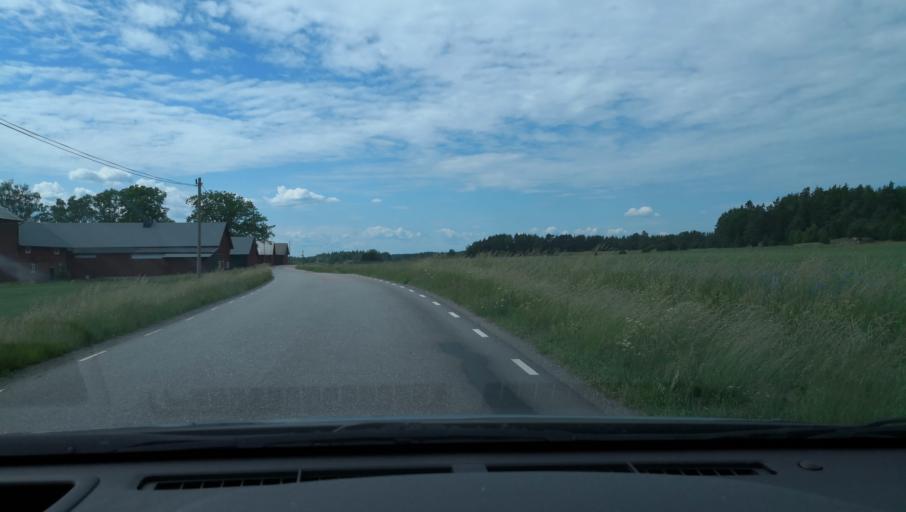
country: SE
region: Uppsala
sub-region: Uppsala Kommun
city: Uppsala
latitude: 59.8121
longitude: 17.5100
